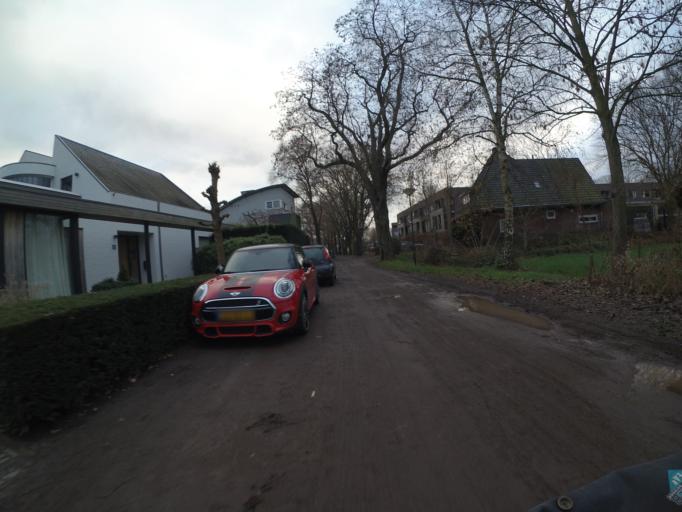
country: NL
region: North Brabant
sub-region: Gemeente Vught
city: Vught
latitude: 51.6469
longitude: 5.2790
